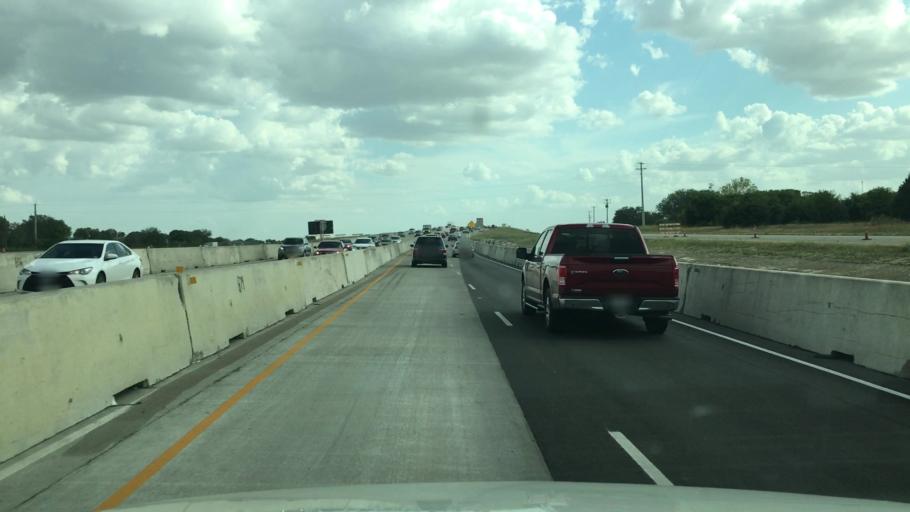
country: US
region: Texas
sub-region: McLennan County
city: Bruceville-Eddy
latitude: 31.2870
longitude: -97.2560
